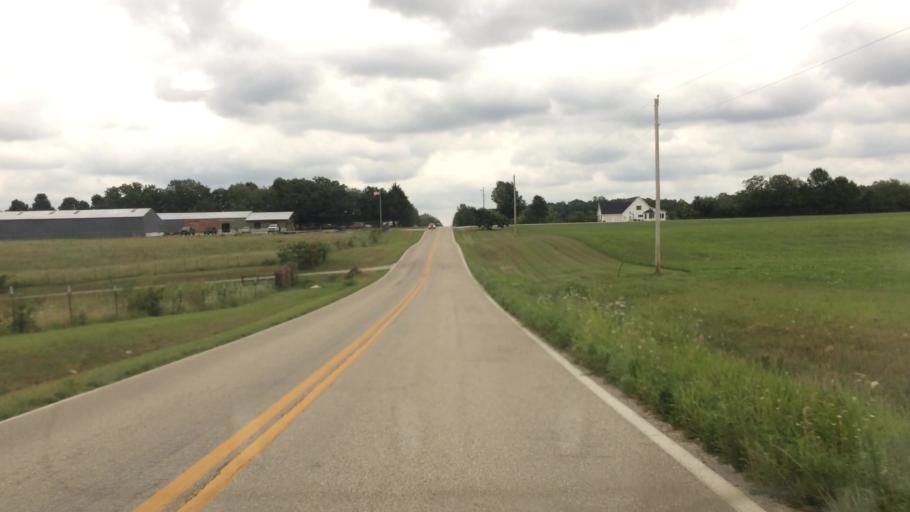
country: US
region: Missouri
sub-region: Greene County
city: Strafford
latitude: 37.2998
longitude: -93.1427
